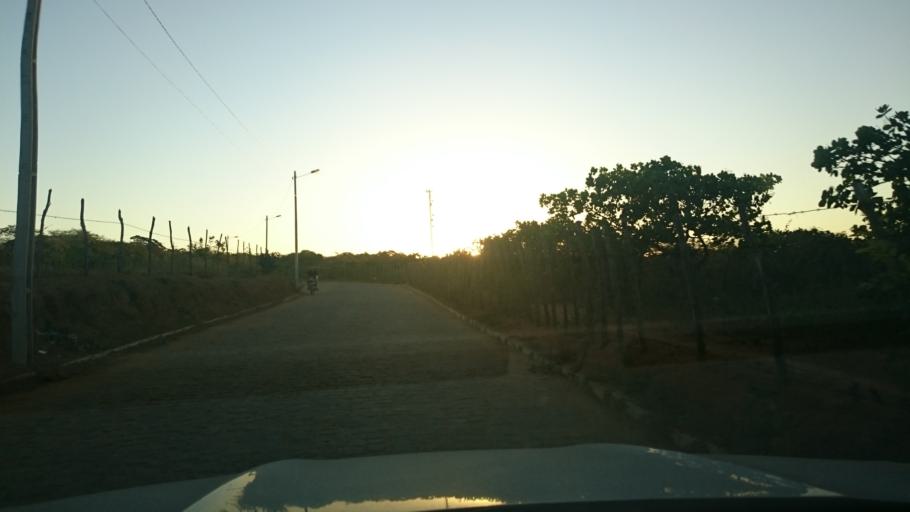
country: BR
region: Rio Grande do Norte
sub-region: Umarizal
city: Umarizal
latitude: -6.0222
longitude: -37.9943
